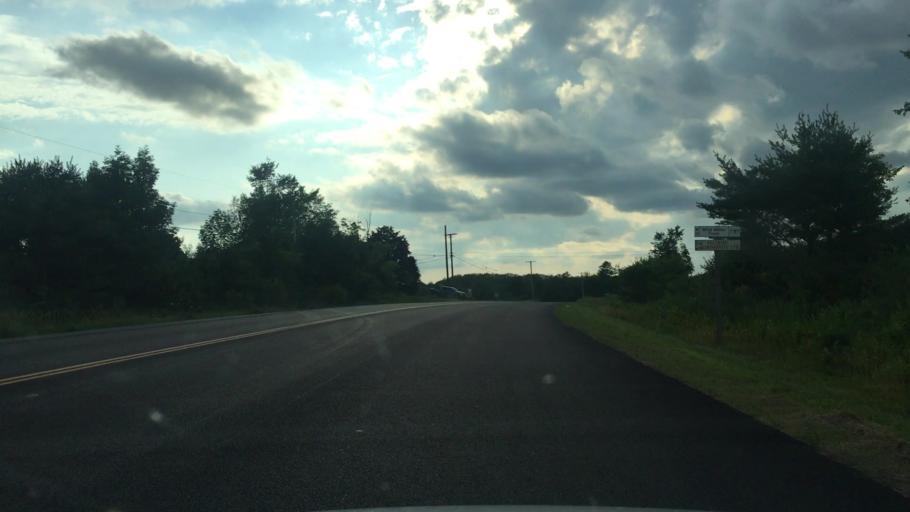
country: US
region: Maine
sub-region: Waldo County
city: Palermo
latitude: 44.3764
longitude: -69.4461
